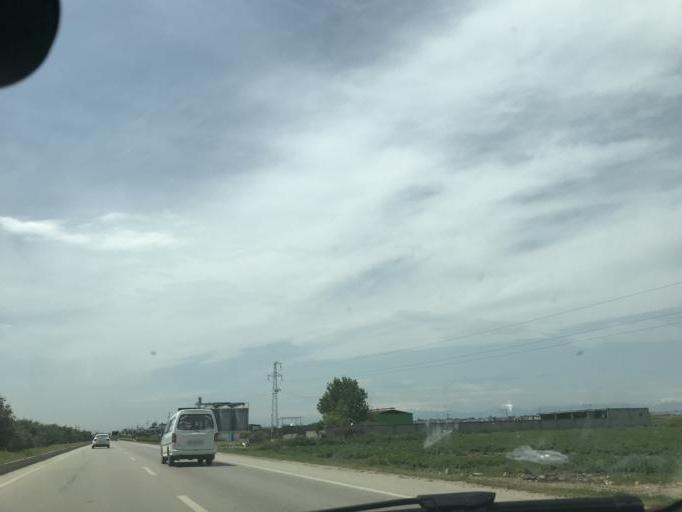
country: TR
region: Adana
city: Yuregir
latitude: 36.9773
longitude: 35.4738
